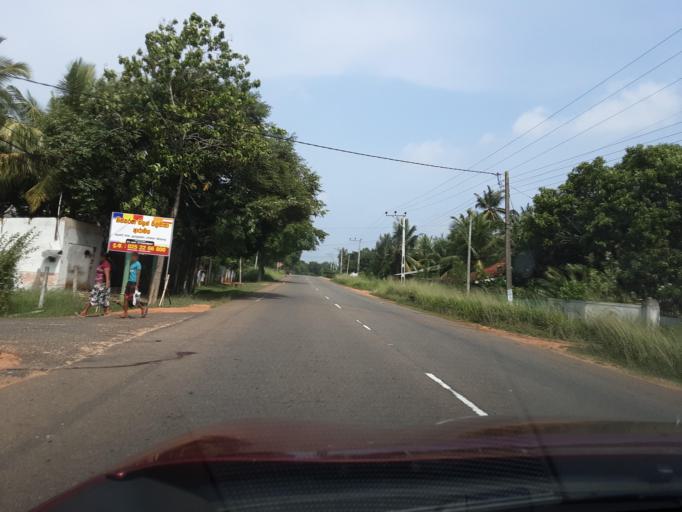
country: LK
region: North Central
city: Anuradhapura
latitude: 8.3327
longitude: 80.5011
